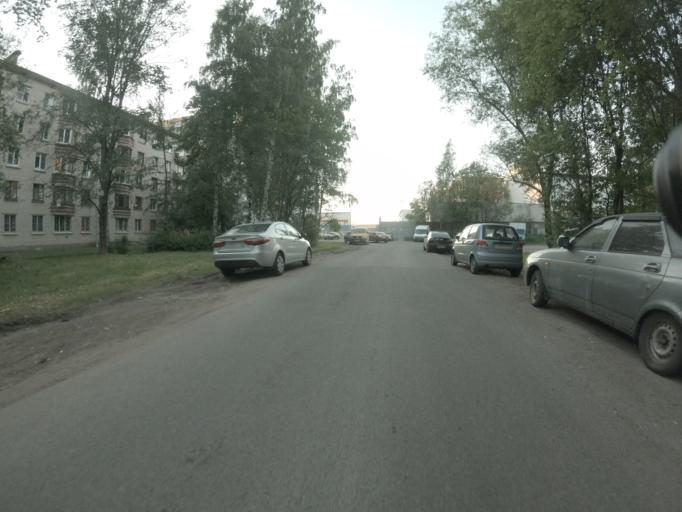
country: RU
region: St.-Petersburg
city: Krasnogvargeisky
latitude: 59.9783
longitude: 30.5146
